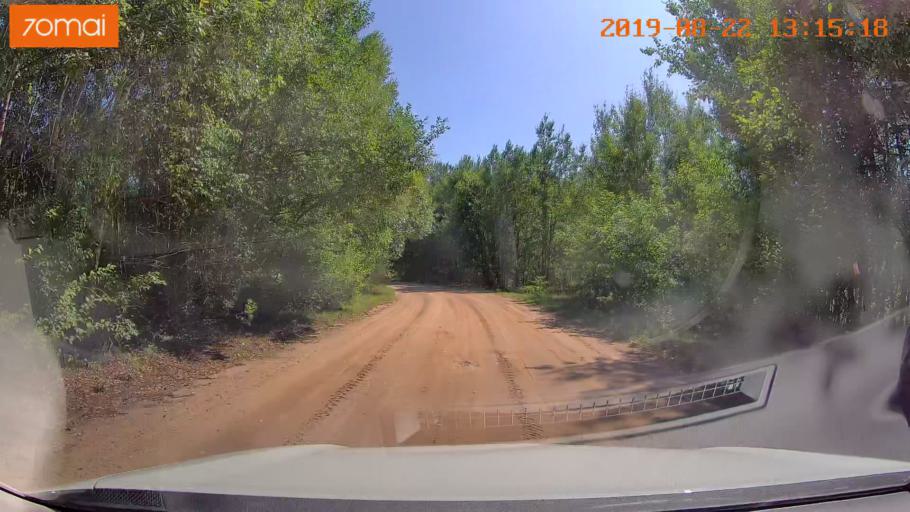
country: BY
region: Minsk
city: Prawdzinski
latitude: 53.2610
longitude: 27.8950
